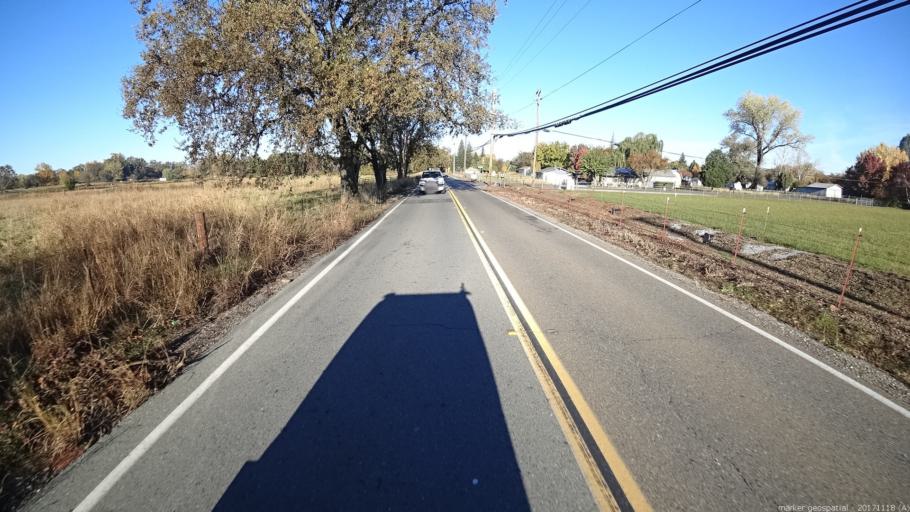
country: US
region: California
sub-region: Shasta County
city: Anderson
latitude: 40.4528
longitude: -122.2702
